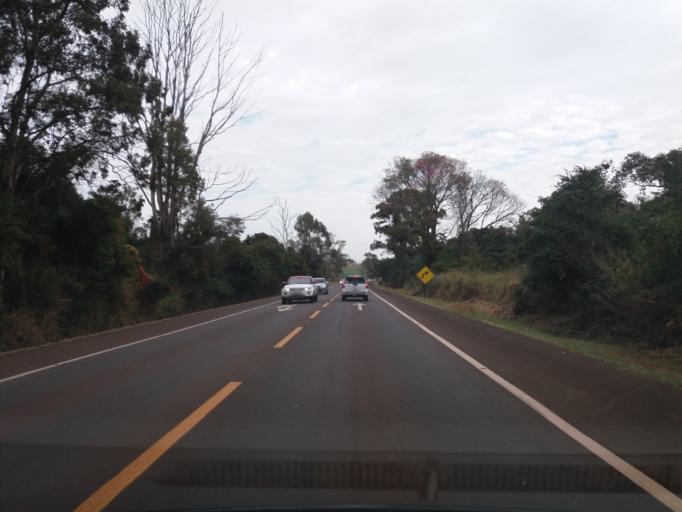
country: BR
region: Parana
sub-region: Campo Mourao
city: Campo Mourao
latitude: -24.3172
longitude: -52.6234
